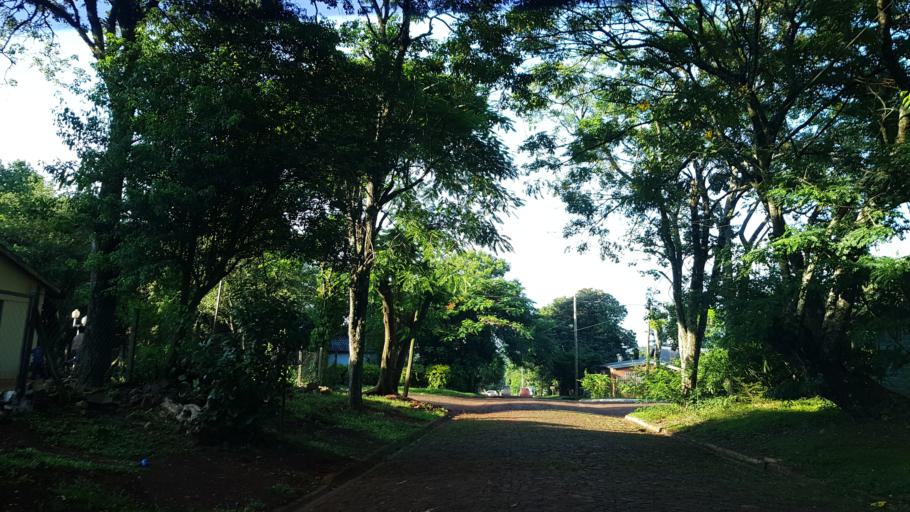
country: AR
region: Misiones
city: Puerto Libertad
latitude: -25.9223
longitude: -54.5864
